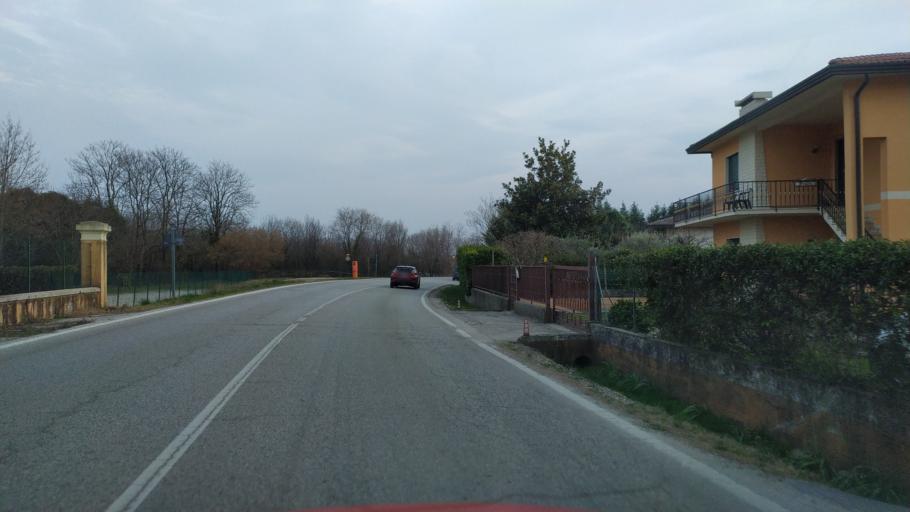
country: IT
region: Veneto
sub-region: Provincia di Vicenza
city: Montecchio Precalcino
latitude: 45.6710
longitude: 11.5621
